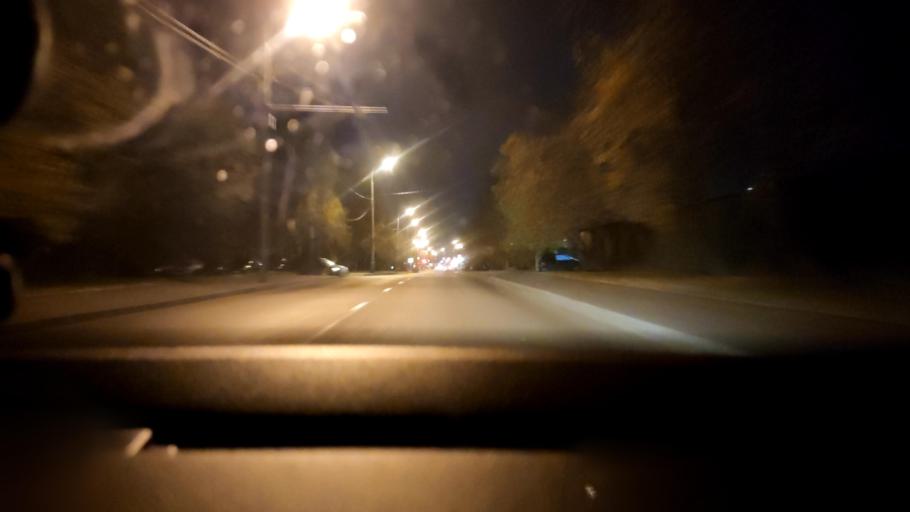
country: RU
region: Moscow
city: Ivanovskoye
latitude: 55.7640
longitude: 37.8400
